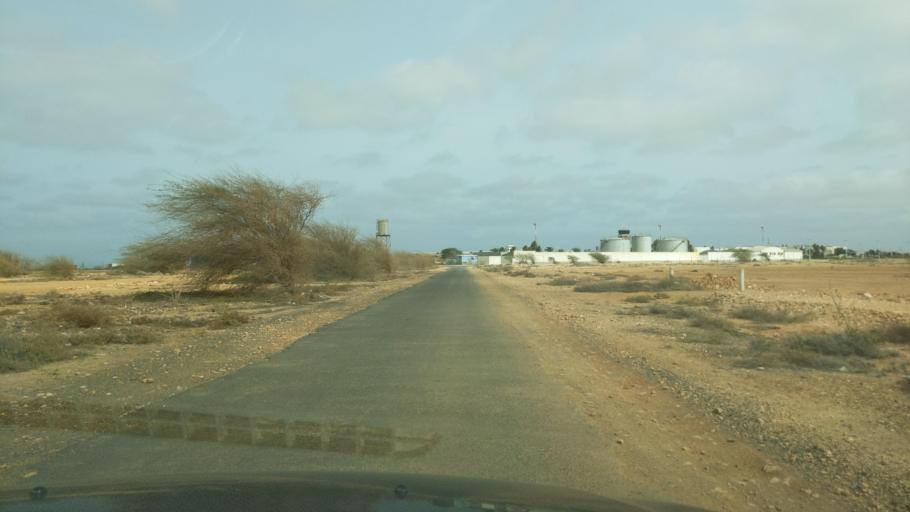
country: CV
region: Sal
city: Espargos
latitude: 16.7299
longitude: -22.9399
